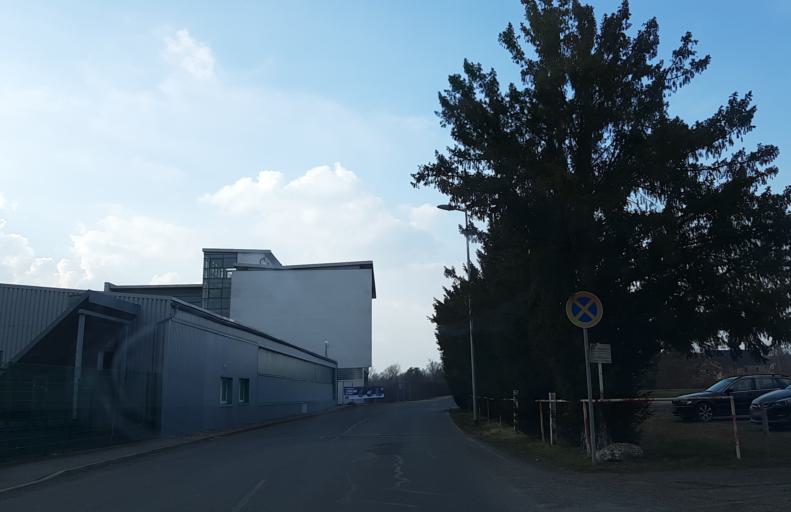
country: DE
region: Saxony
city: Wildenhain
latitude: 51.2899
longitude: 13.5005
